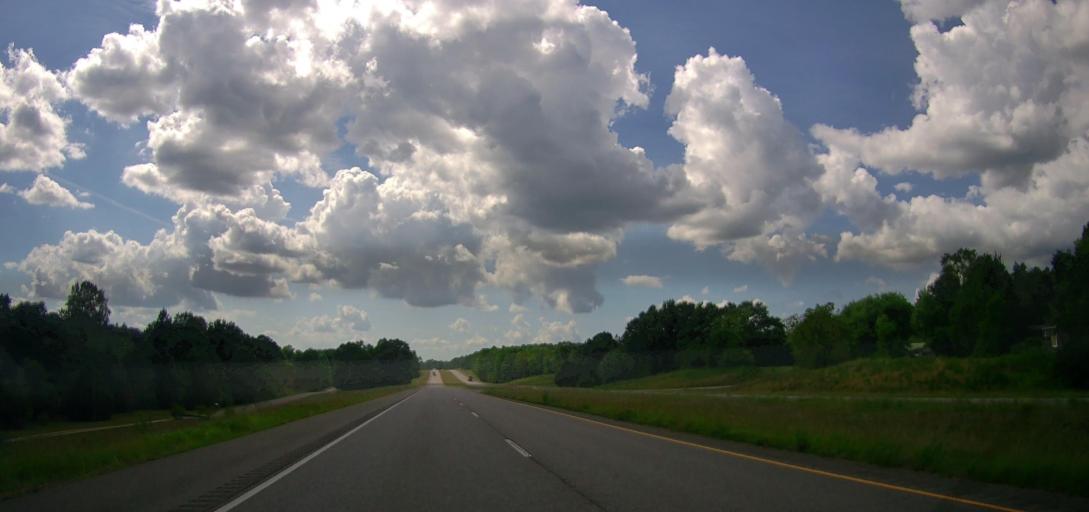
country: US
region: Alabama
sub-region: Pickens County
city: Reform
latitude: 33.3993
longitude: -88.0641
